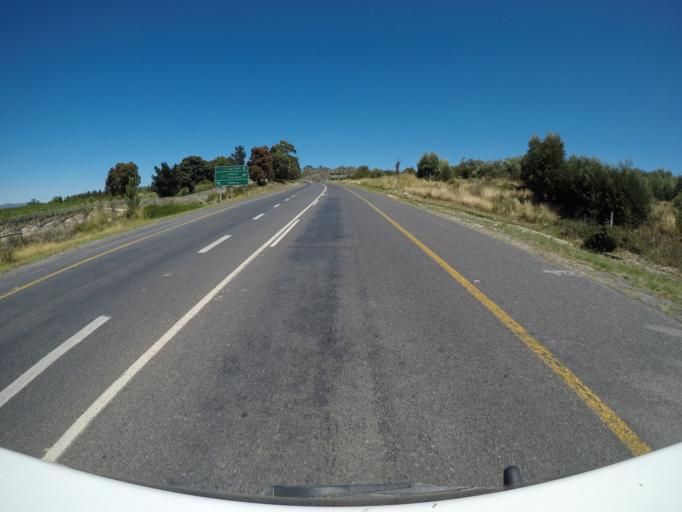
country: ZA
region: Western Cape
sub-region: Overberg District Municipality
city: Grabouw
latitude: -34.1623
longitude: 19.0126
